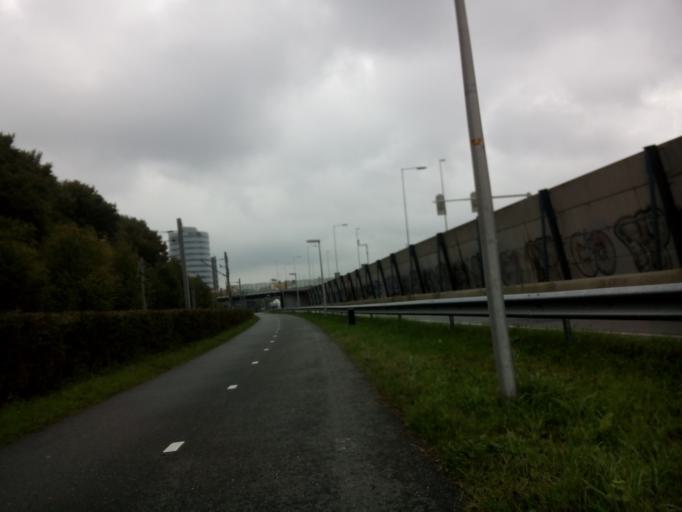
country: NL
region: South Holland
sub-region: Gemeente Zoetermeer
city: Zoetermeer
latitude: 52.0488
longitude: 4.4715
